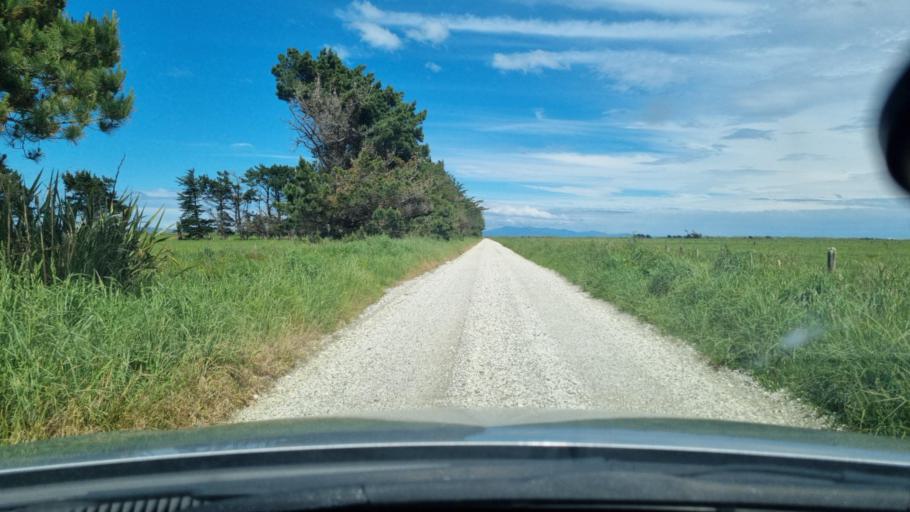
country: NZ
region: Southland
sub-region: Invercargill City
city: Invercargill
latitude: -46.3833
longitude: 168.2671
